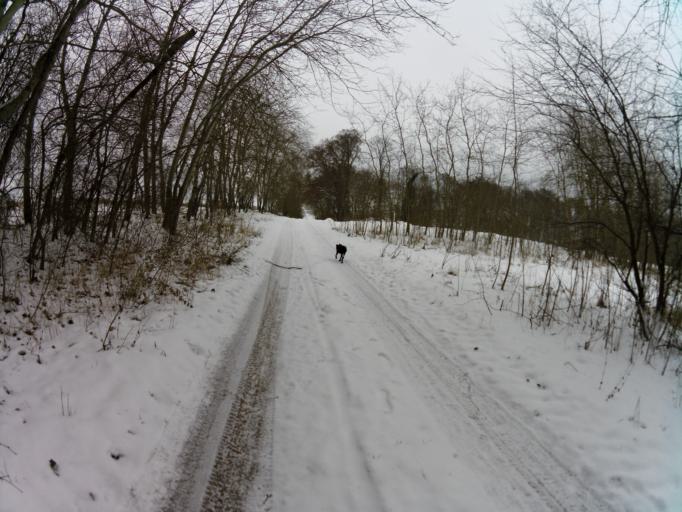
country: PL
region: West Pomeranian Voivodeship
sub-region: Powiat choszczenski
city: Recz
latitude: 53.3409
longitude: 15.5408
